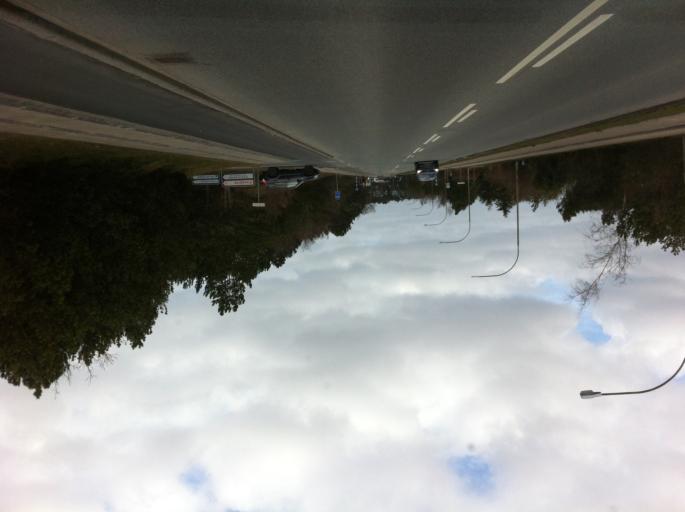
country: DK
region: Central Jutland
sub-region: Syddjurs Kommune
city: Ebeltoft
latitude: 56.1875
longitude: 10.6827
